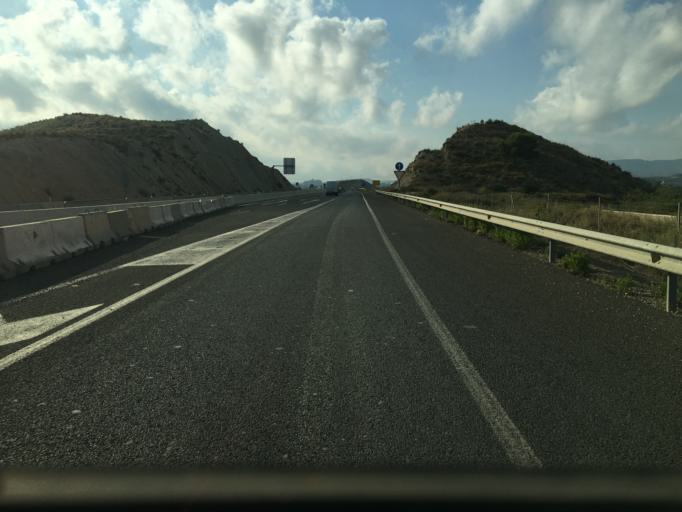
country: ES
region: Murcia
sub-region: Murcia
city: Beniel
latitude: 38.0008
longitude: -1.0115
